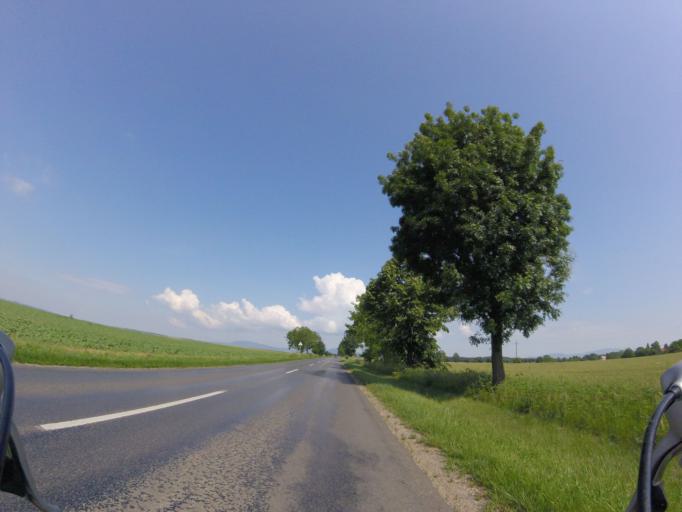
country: HU
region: Baranya
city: Kozarmisleny
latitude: 45.9995
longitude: 18.3178
